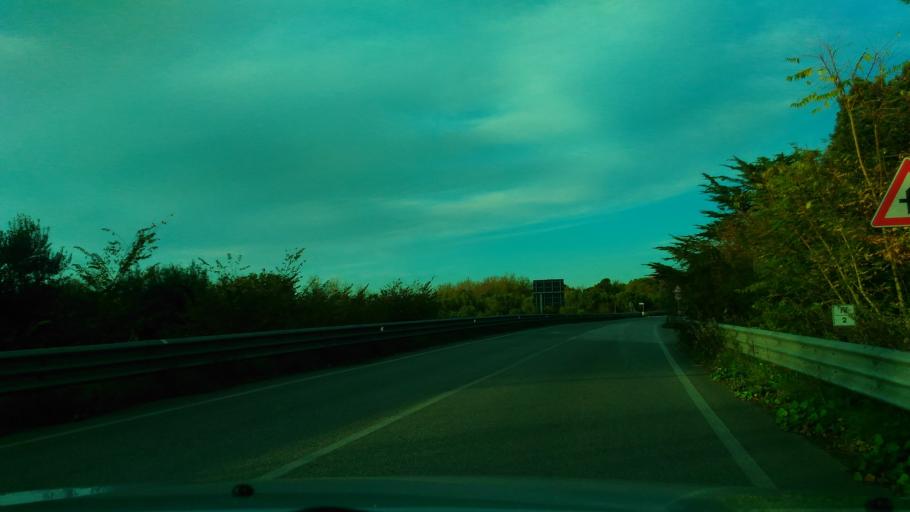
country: IT
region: Tuscany
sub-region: Provincia di Livorno
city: S.P. in Palazzi
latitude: 43.3483
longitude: 10.5039
